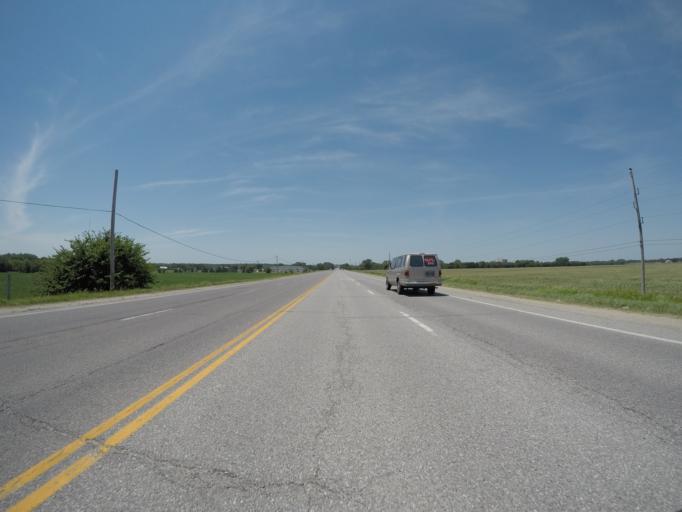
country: US
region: Kansas
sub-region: Geary County
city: Grandview Plaza
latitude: 39.0283
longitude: -96.8070
